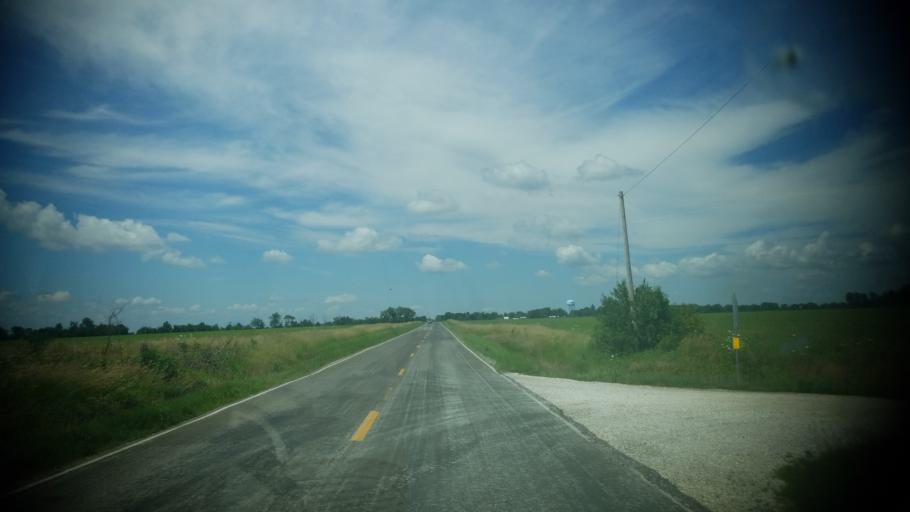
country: US
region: Missouri
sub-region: Audrain County
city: Vandalia
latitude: 39.3308
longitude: -91.3451
